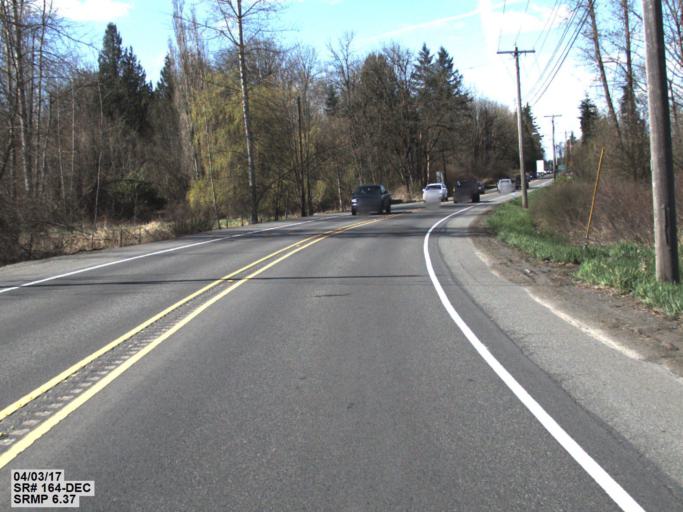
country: US
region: Washington
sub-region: King County
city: Lake Morton-Berrydale
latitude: 47.2567
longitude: -122.1247
